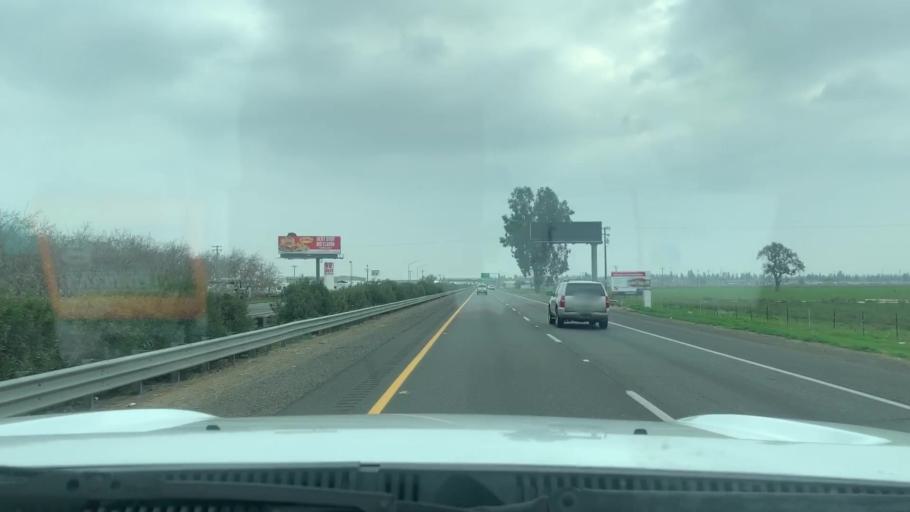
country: US
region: California
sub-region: Tulare County
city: Tulare
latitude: 36.2484
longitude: -119.3517
